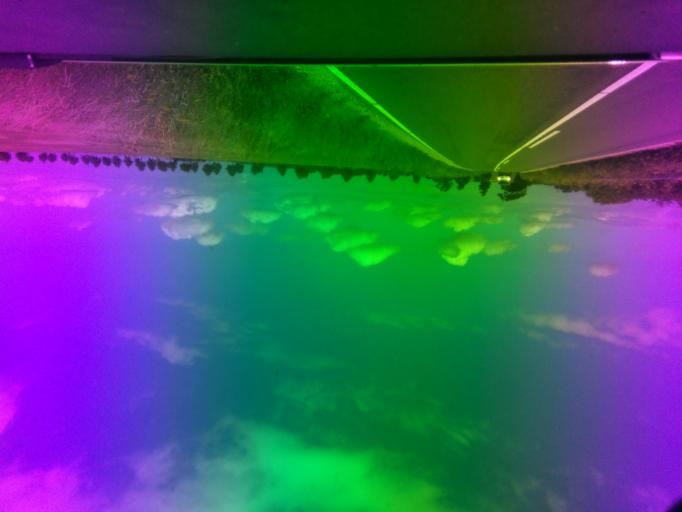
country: DK
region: Zealand
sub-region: Kalundborg Kommune
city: Svebolle
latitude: 55.5870
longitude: 11.3167
